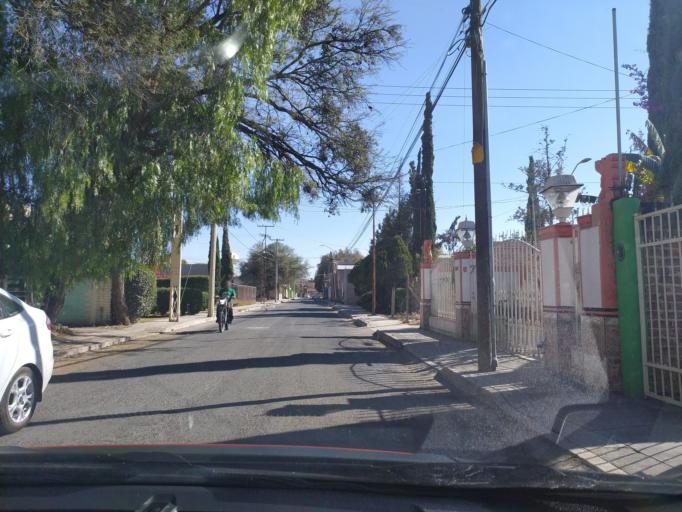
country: MX
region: Guanajuato
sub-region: San Francisco del Rincon
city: Estacion de San Francisco
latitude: 21.0258
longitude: -101.8325
